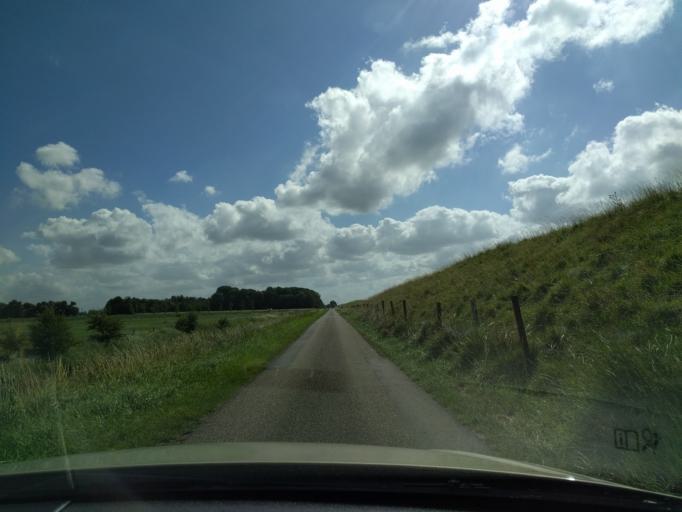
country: NL
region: Zeeland
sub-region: Gemeente Veere
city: Veere
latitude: 51.5304
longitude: 3.6756
